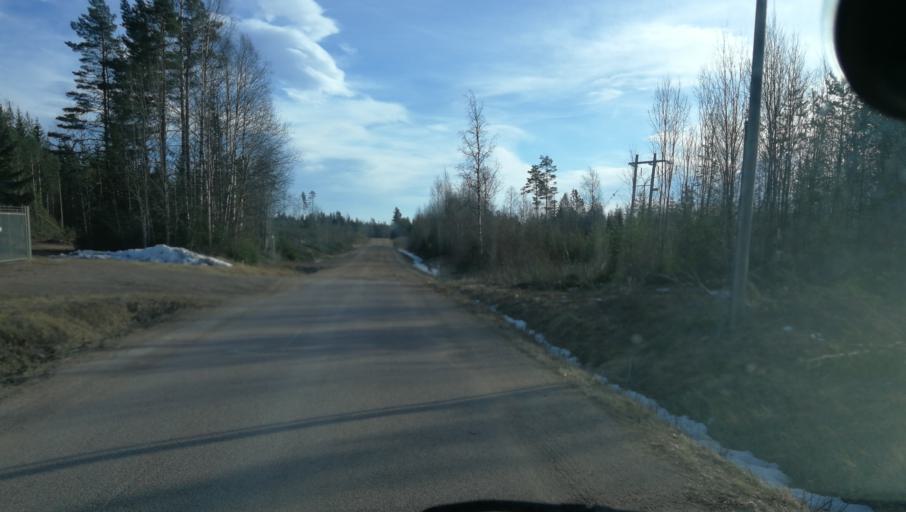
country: SE
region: Dalarna
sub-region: Vansbro Kommun
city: Vansbro
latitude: 60.8274
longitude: 14.1942
